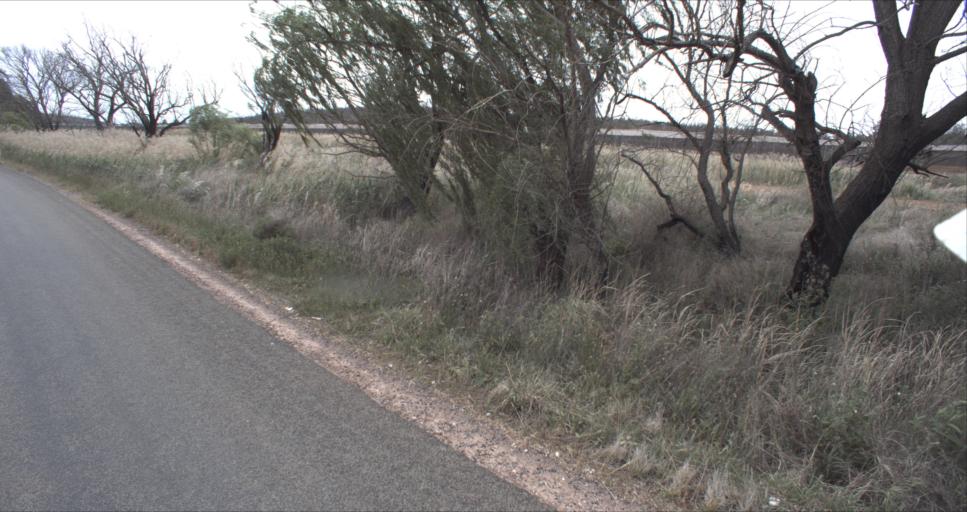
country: AU
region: New South Wales
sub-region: Leeton
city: Leeton
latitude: -34.4296
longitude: 146.3778
